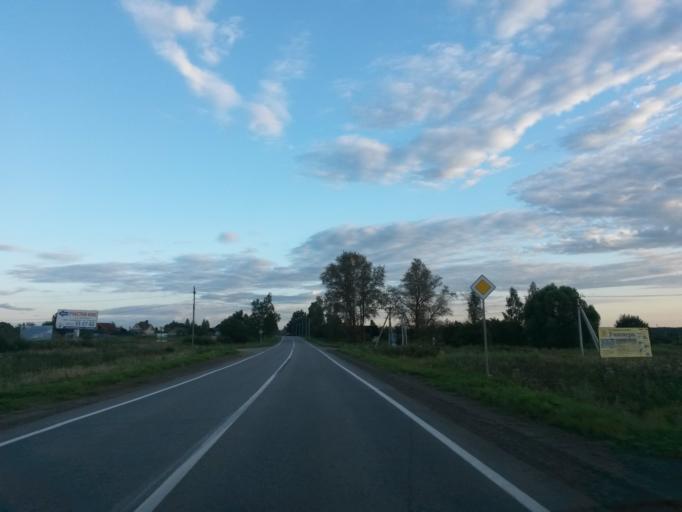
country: RU
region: Jaroslavl
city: Gavrilov-Yam
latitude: 57.3550
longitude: 39.9082
